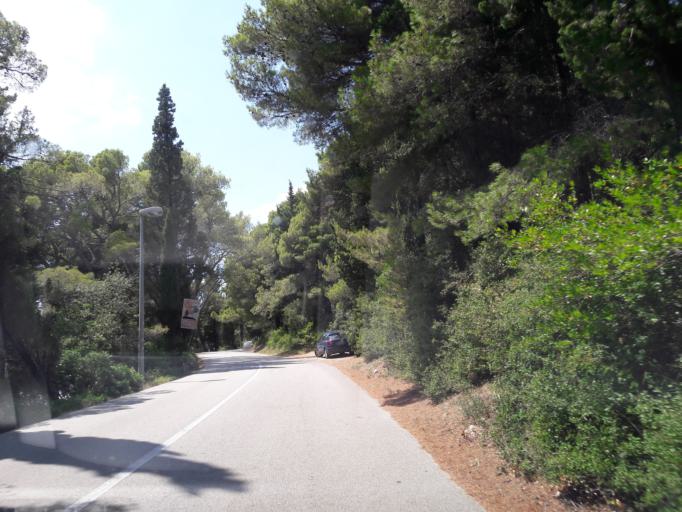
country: HR
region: Dubrovacko-Neretvanska
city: Korcula
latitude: 42.9746
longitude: 17.1541
